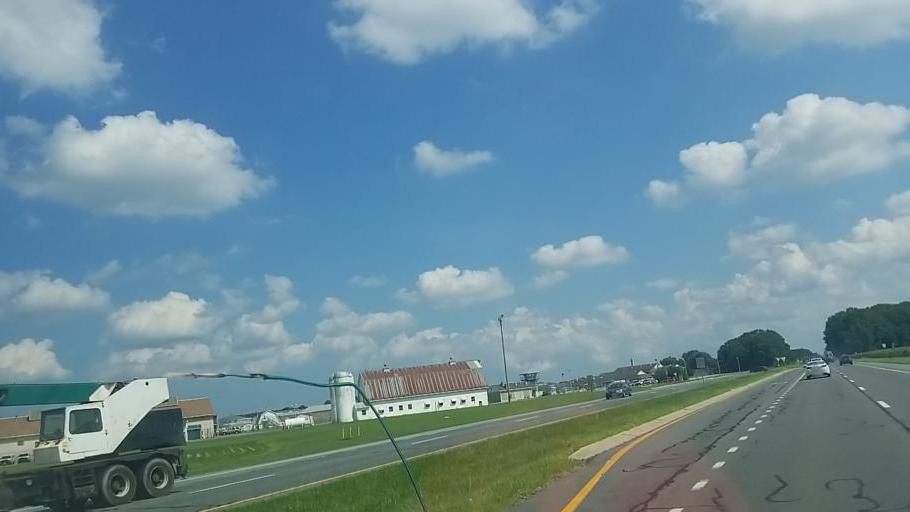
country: US
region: Delaware
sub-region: Sussex County
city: Georgetown
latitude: 38.6607
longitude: -75.3755
